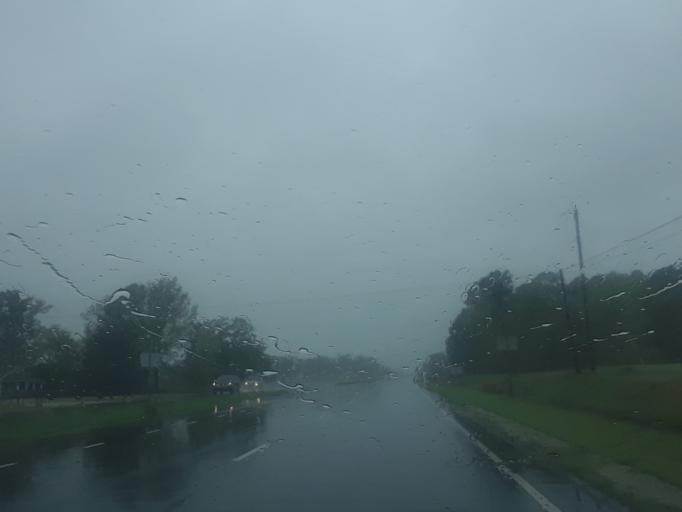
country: US
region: North Carolina
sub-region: Harnett County
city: Erwin
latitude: 35.3609
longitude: -78.7000
